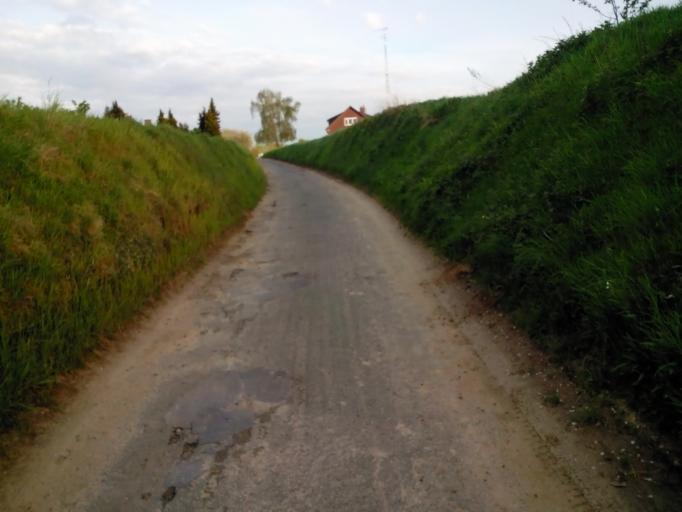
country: BE
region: Flanders
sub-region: Provincie Vlaams-Brabant
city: Leuven
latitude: 50.8601
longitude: 4.7234
